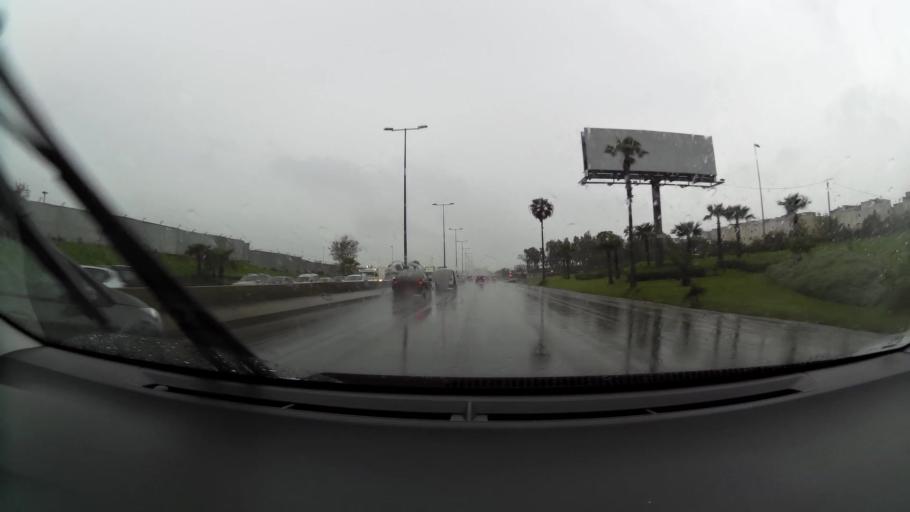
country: MA
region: Grand Casablanca
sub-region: Casablanca
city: Casablanca
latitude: 33.5737
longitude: -7.5644
